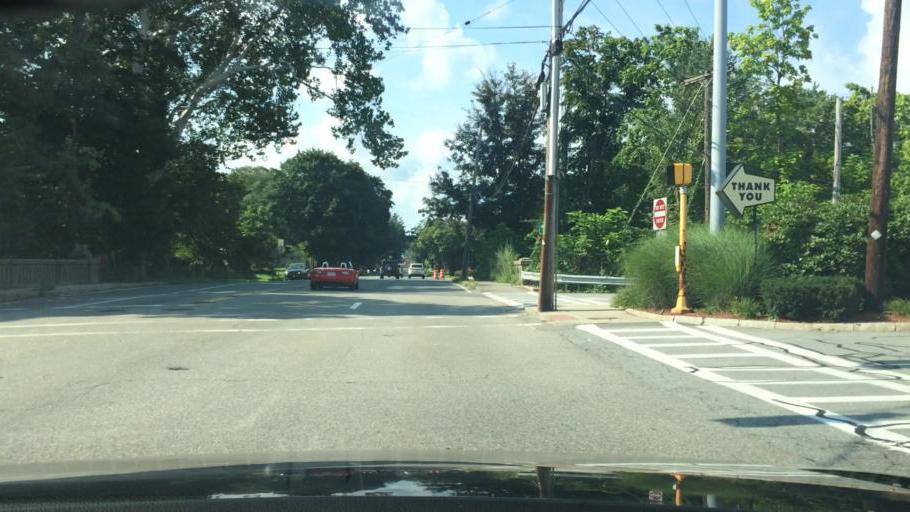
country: US
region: Massachusetts
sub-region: Essex County
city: Andover
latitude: 42.6645
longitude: -71.1458
